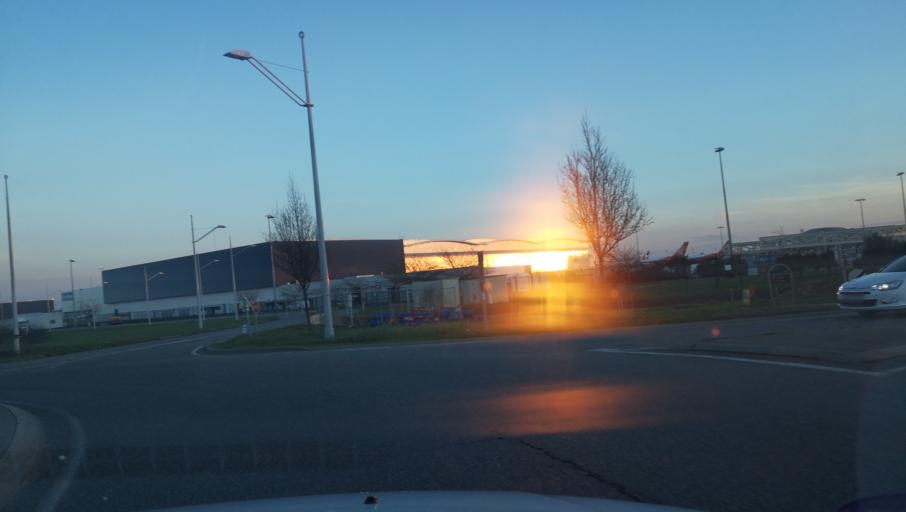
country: FR
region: Midi-Pyrenees
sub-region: Departement de la Haute-Garonne
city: Cornebarrieu
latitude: 43.6605
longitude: 1.3478
